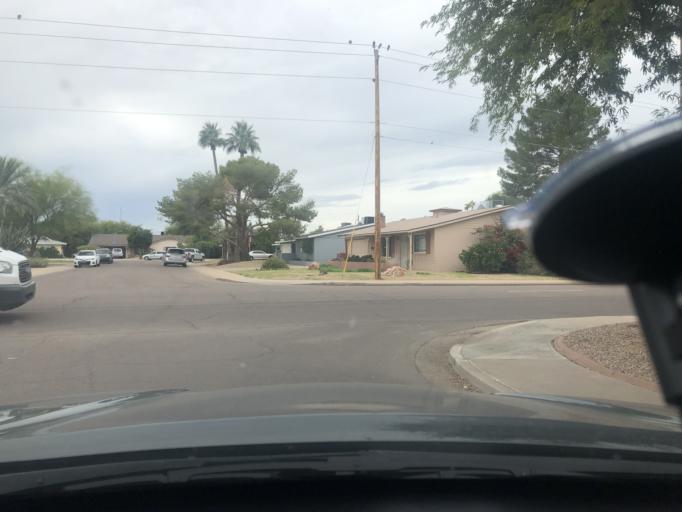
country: US
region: Arizona
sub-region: Maricopa County
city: Scottsdale
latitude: 33.4893
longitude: -111.8958
